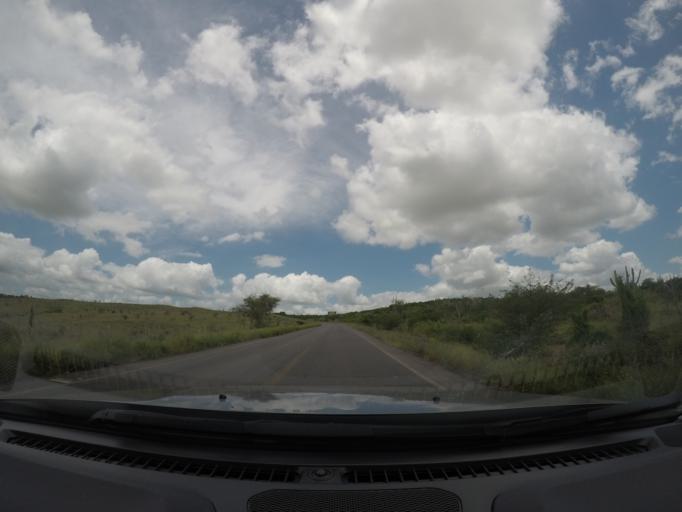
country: BR
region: Bahia
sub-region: Ipira
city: Ipira
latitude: -12.2550
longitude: -39.8192
